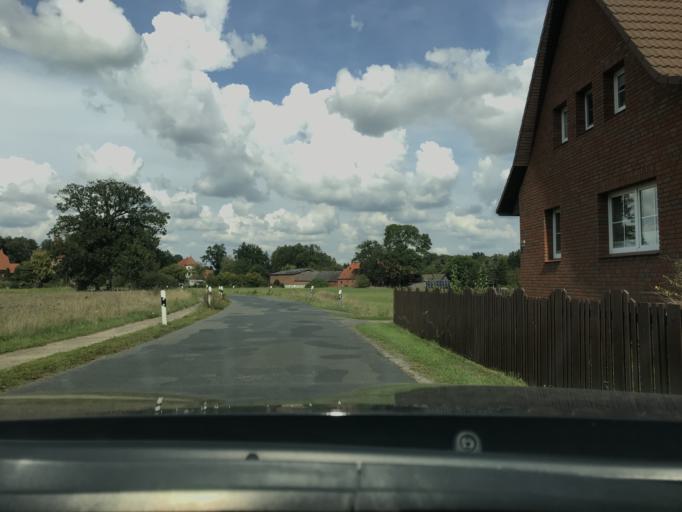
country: DE
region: Lower Saxony
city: Suderburg
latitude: 52.8912
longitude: 10.4527
